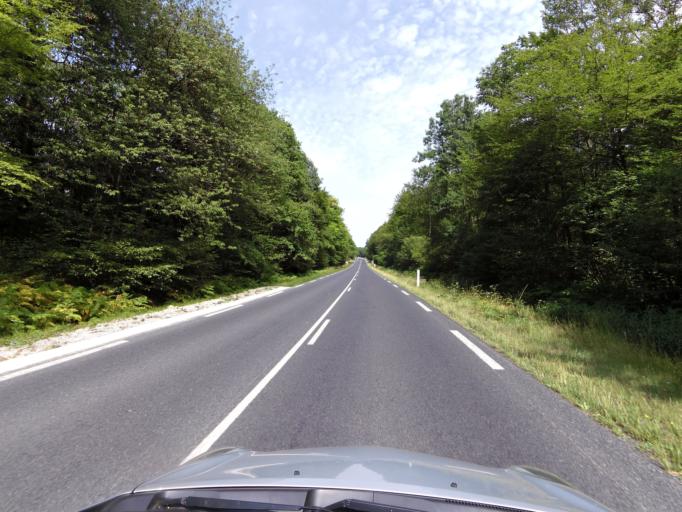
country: FR
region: Champagne-Ardenne
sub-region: Departement de la Marne
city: Rilly-la-Montagne
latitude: 49.1482
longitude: 4.0075
